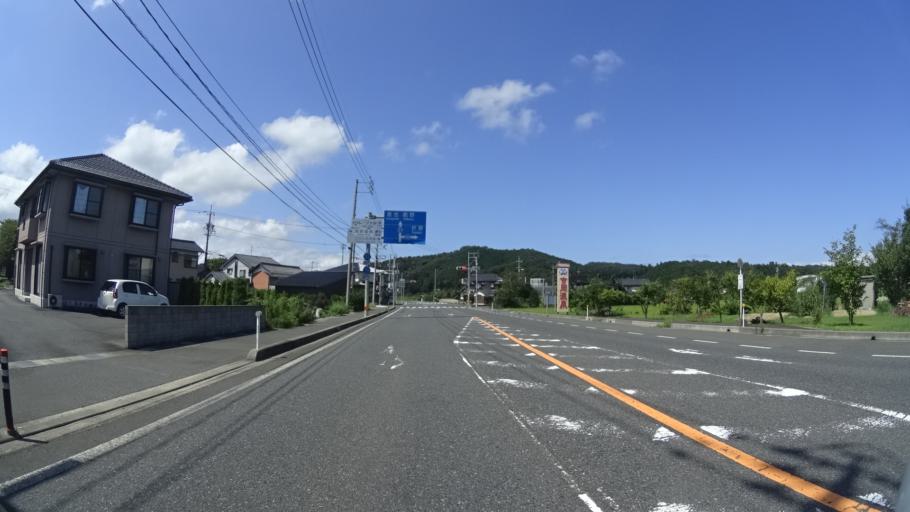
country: JP
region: Tottori
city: Tottori
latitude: 35.4961
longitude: 134.1344
